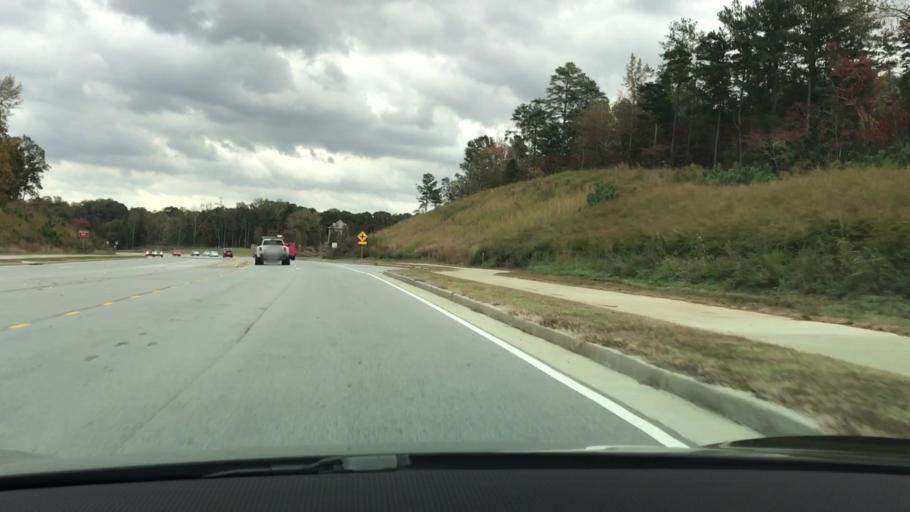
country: US
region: Georgia
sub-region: Hall County
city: Flowery Branch
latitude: 34.1099
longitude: -83.8643
